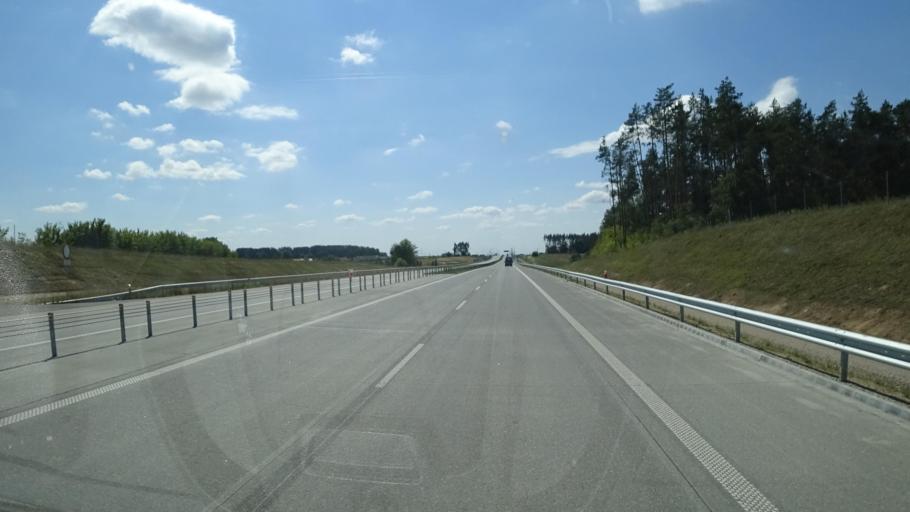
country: PL
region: Podlasie
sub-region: Powiat lomzynski
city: Piatnica
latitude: 53.2806
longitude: 22.1362
